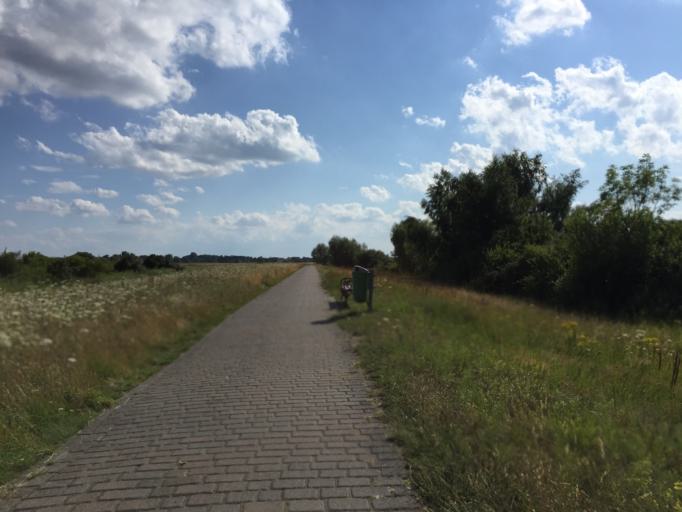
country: DE
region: Mecklenburg-Vorpommern
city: Hiddensee
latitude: 54.5835
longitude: 13.1098
